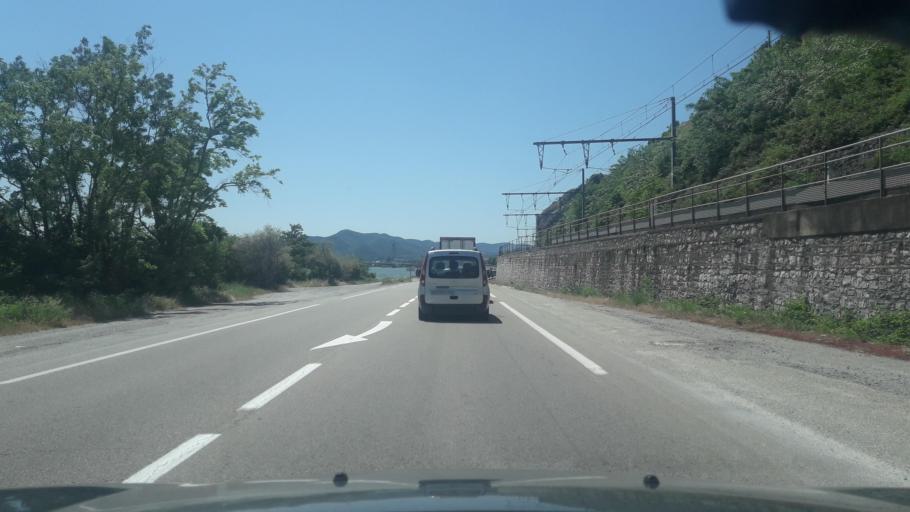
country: FR
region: Rhone-Alpes
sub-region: Departement de l'Ardeche
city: Le Pouzin
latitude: 44.7677
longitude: 4.7539
